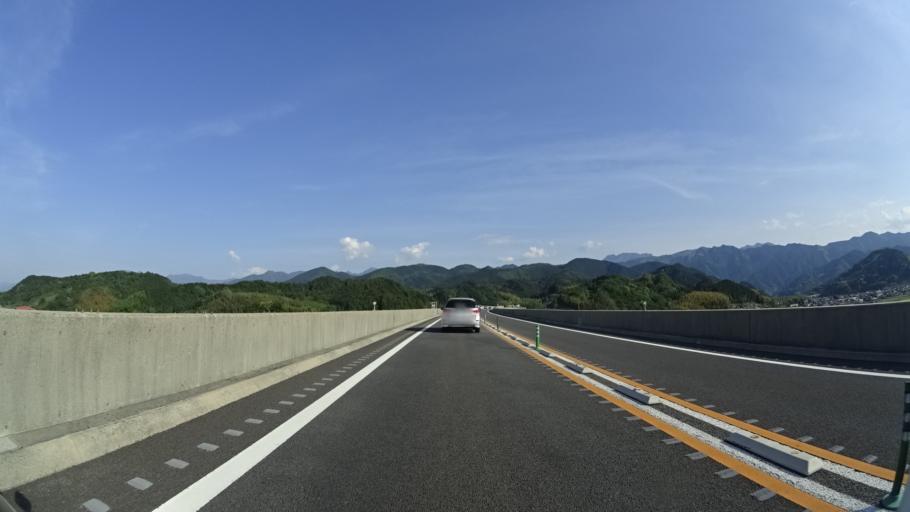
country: JP
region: Ehime
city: Saijo
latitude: 33.8913
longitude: 133.0849
